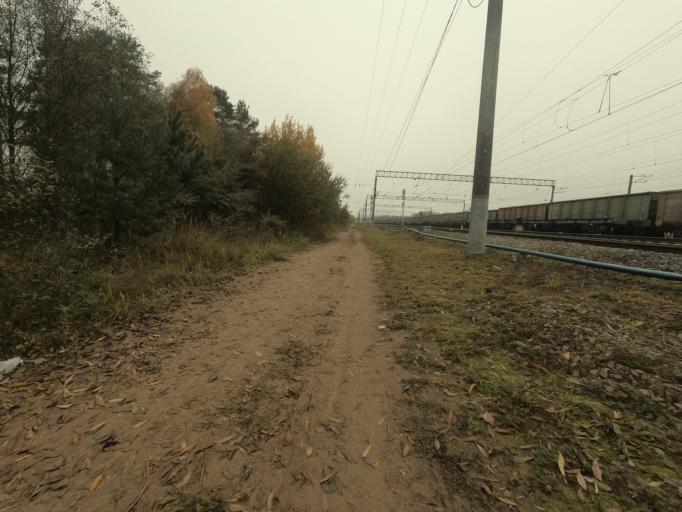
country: RU
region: Leningrad
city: Pavlovo
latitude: 59.7665
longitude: 30.9549
